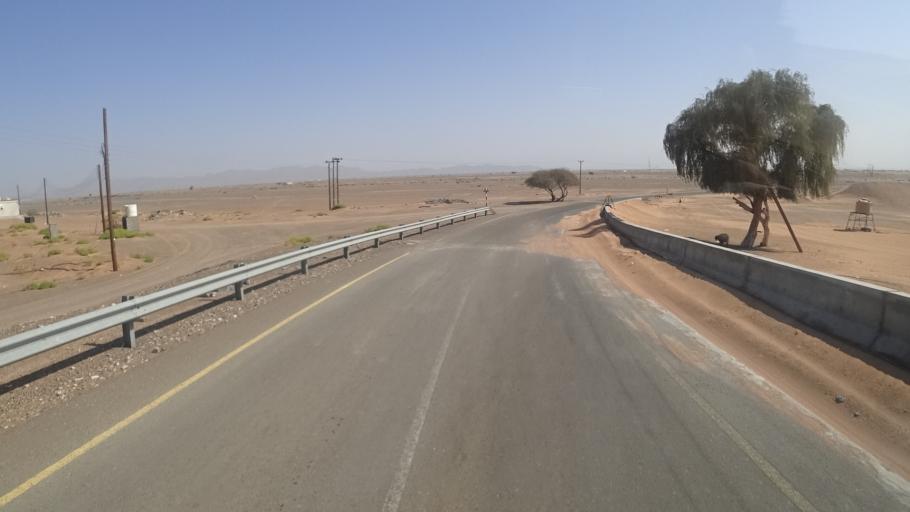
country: OM
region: Ash Sharqiyah
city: Al Qabil
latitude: 22.5004
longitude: 58.7169
